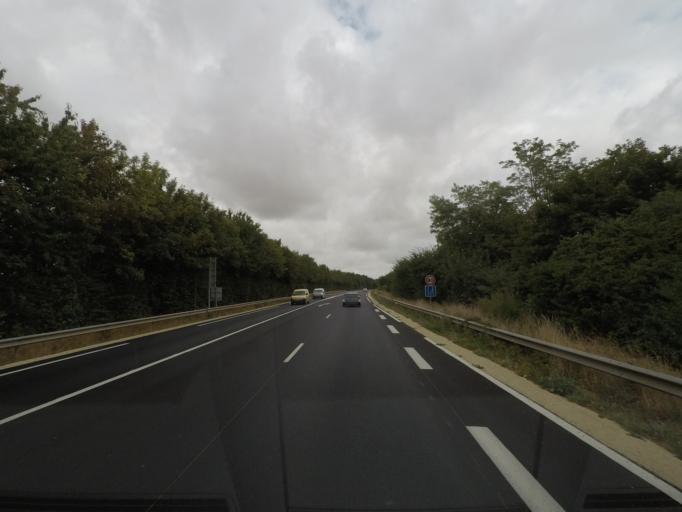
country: FR
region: Poitou-Charentes
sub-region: Departement des Deux-Sevres
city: Celles-sur-Belle
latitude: 46.2567
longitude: -0.2258
